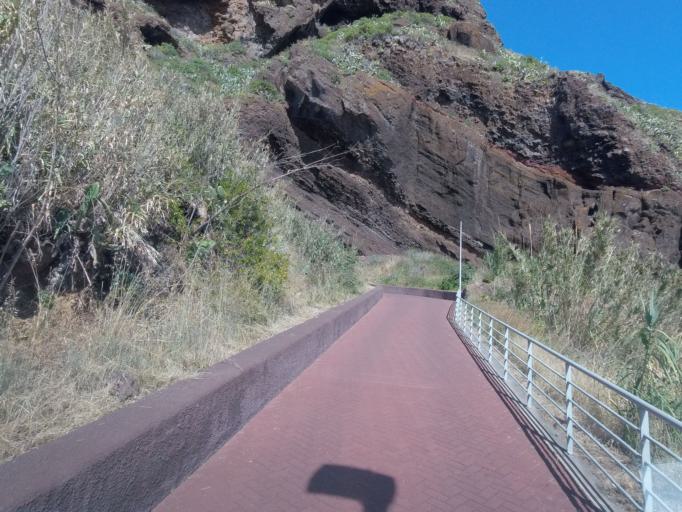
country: PT
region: Madeira
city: Canico
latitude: 32.6393
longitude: -16.8529
